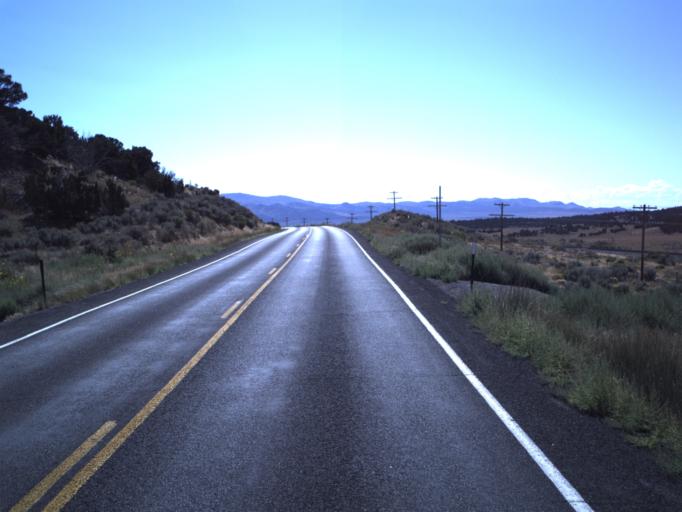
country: US
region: Utah
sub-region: Utah County
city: Genola
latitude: 39.9492
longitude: -112.2350
